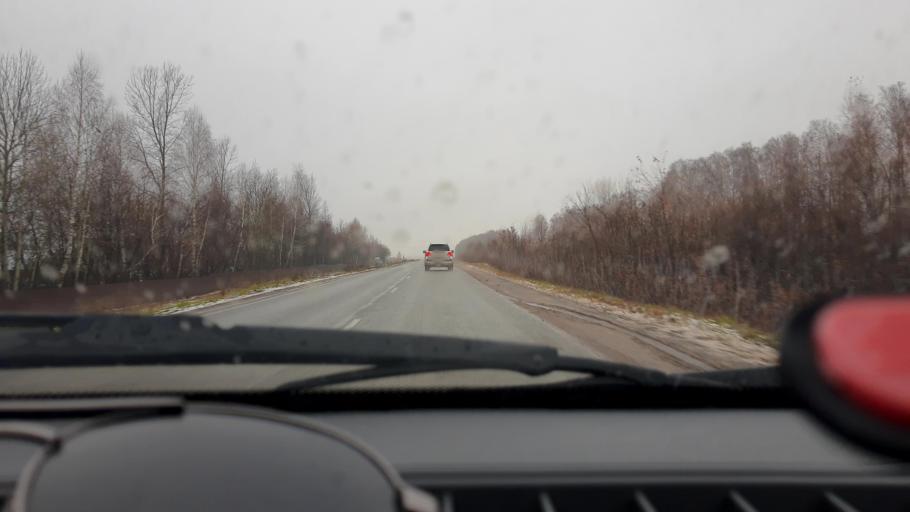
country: RU
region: Bashkortostan
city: Kabakovo
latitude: 54.6017
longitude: 56.2012
